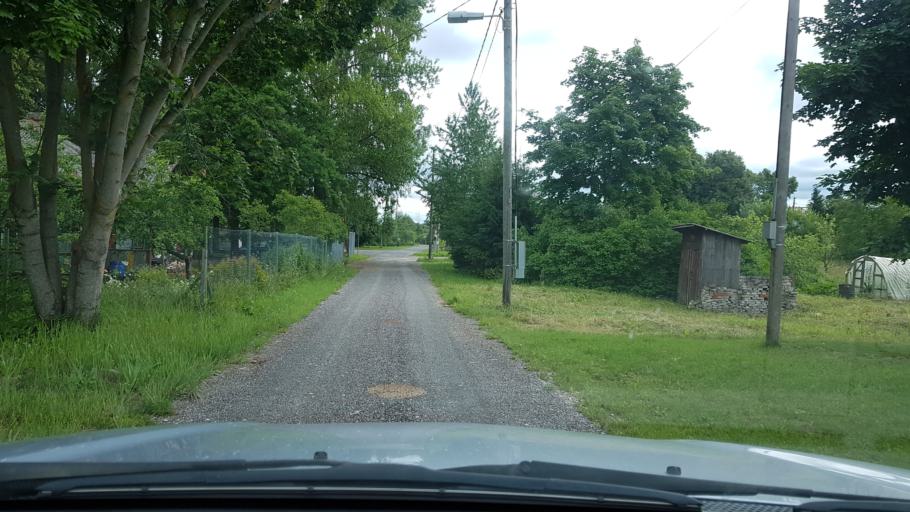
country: EE
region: Ida-Virumaa
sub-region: Sillamaee linn
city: Sillamae
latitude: 59.3726
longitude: 27.7662
